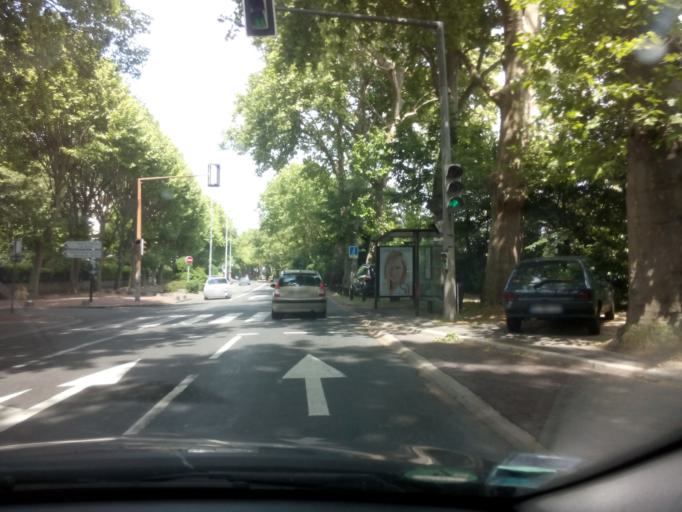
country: FR
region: Ile-de-France
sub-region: Departement des Hauts-de-Seine
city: Saint-Cloud
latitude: 48.8493
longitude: 2.2239
